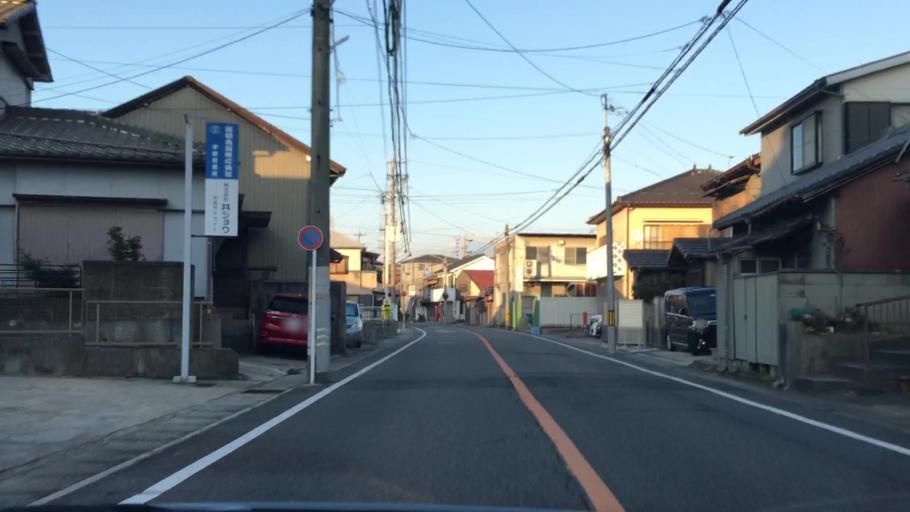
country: JP
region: Aichi
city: Obu
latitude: 35.0731
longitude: 136.9432
